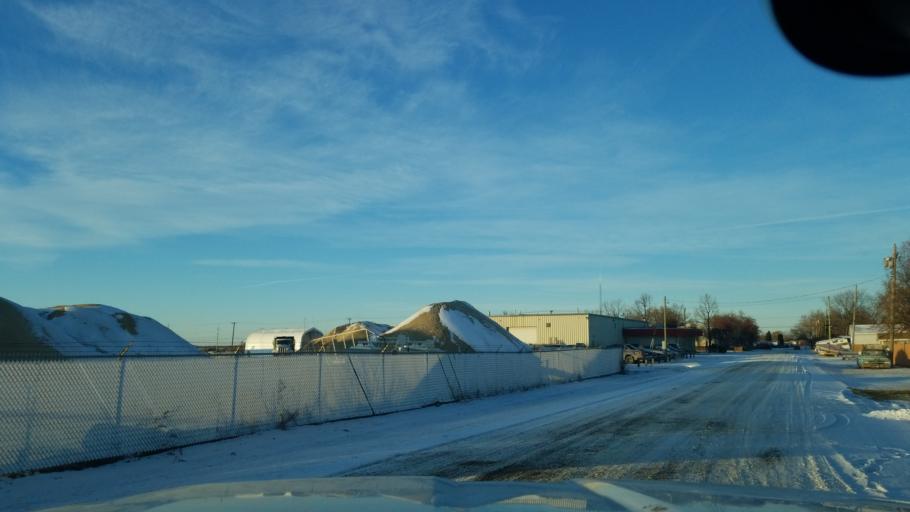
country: CA
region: Manitoba
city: Portage la Prairie
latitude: 49.9798
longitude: -98.3040
